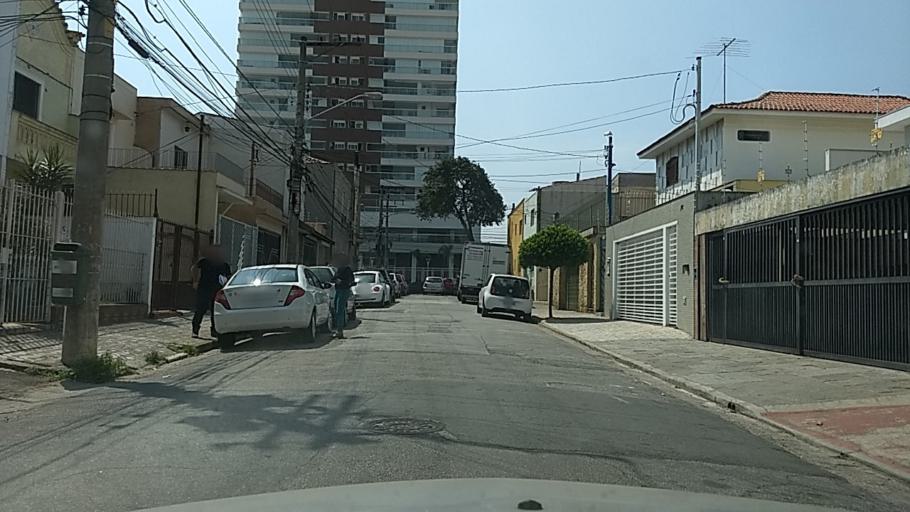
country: BR
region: Sao Paulo
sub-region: Sao Paulo
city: Sao Paulo
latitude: -23.5307
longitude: -46.5659
